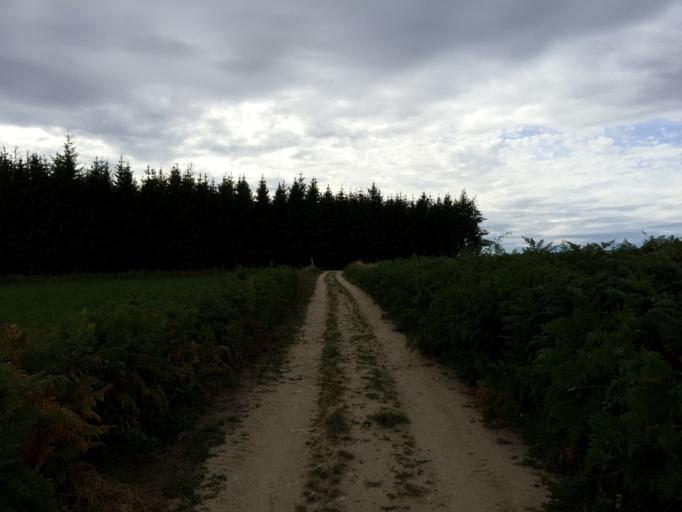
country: FR
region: Rhone-Alpes
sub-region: Departement de la Loire
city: Saint-Bonnet-le-Chateau
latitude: 45.3823
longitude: 4.0386
